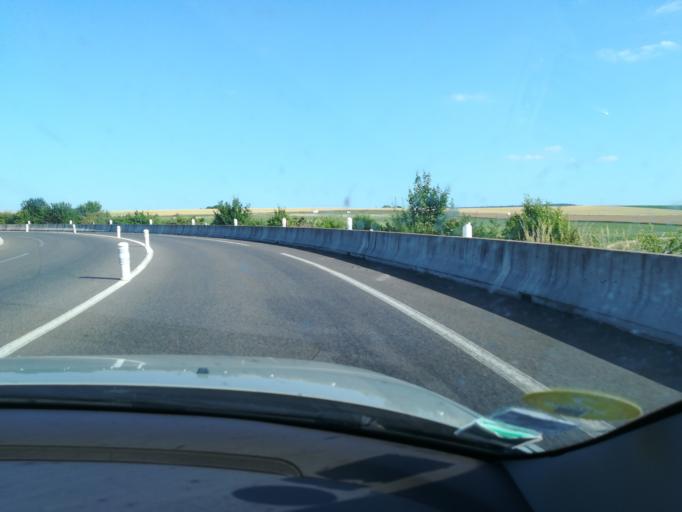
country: FR
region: Champagne-Ardenne
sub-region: Departement de la Marne
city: Bezannes
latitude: 49.2036
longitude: 4.0056
